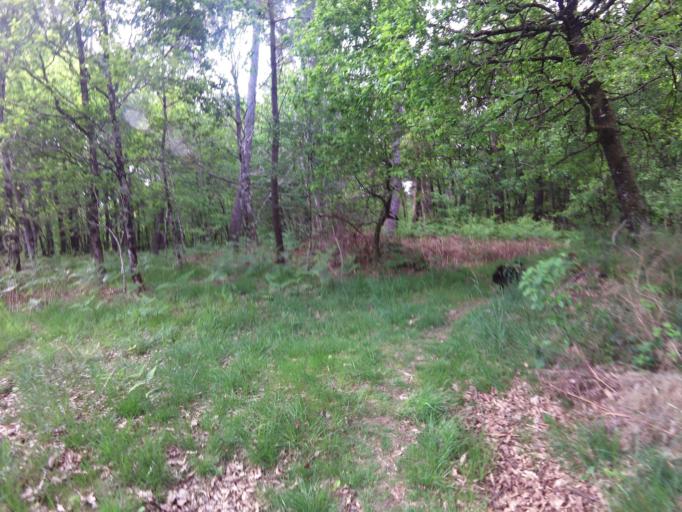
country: FR
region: Brittany
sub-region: Departement du Morbihan
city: Molac
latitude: 47.7603
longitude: -2.4322
